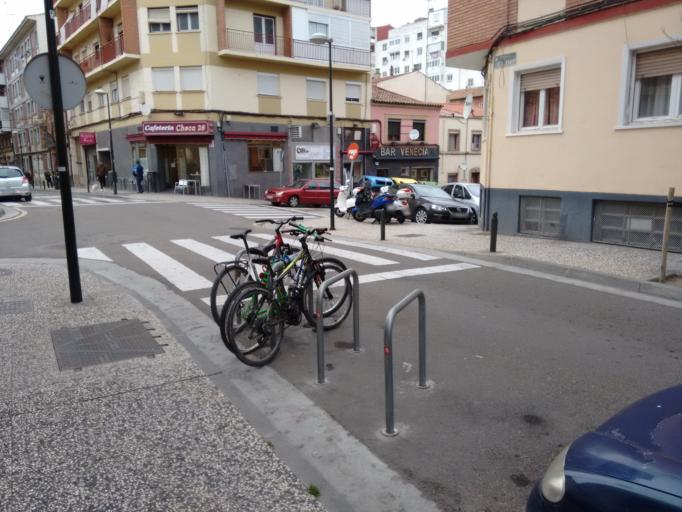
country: ES
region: Aragon
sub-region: Provincia de Zaragoza
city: Zaragoza
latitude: 41.6322
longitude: -0.8868
